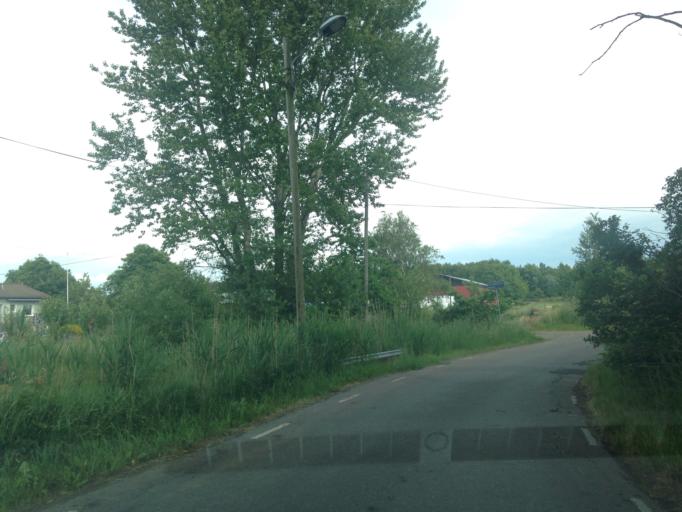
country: SE
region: Vaestra Goetaland
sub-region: Goteborg
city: Majorna
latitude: 57.7584
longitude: 11.8610
